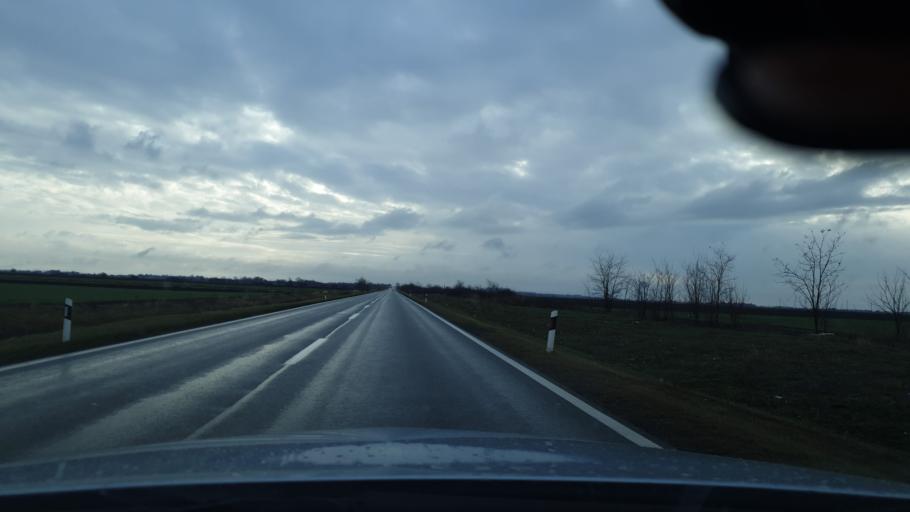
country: RS
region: Autonomna Pokrajina Vojvodina
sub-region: Juznobanatski Okrug
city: Kovin
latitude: 44.7780
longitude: 20.9344
